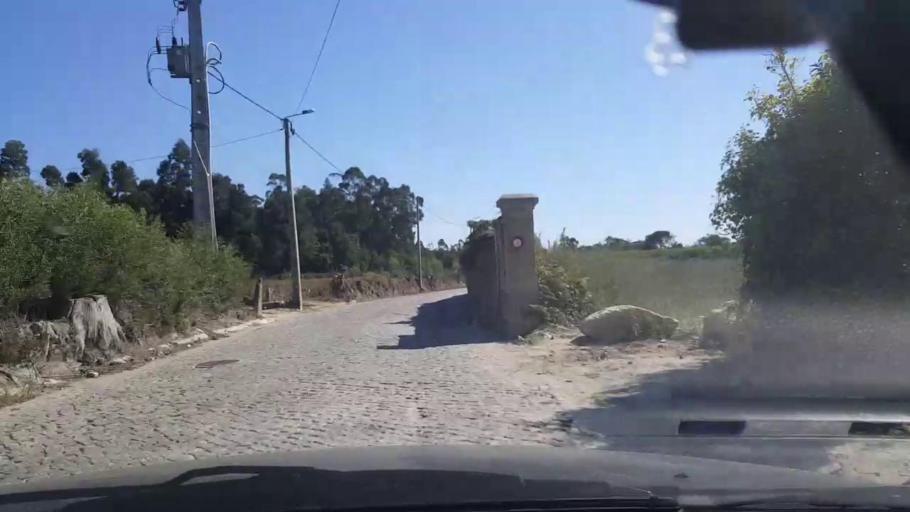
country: PT
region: Porto
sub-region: Vila do Conde
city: Arvore
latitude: 41.3153
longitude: -8.6882
